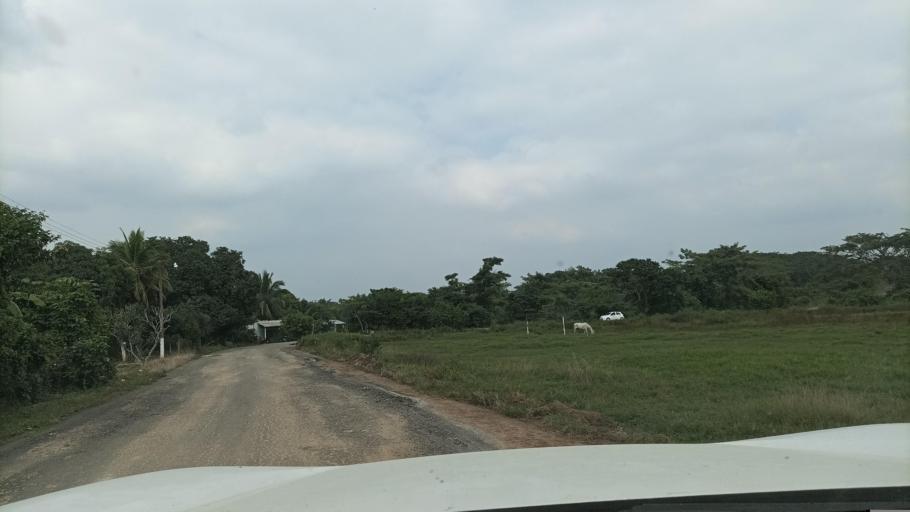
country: MX
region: Veracruz
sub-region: Texistepec
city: San Lorenzo Tenochtitlan
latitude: 17.7734
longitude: -94.8034
